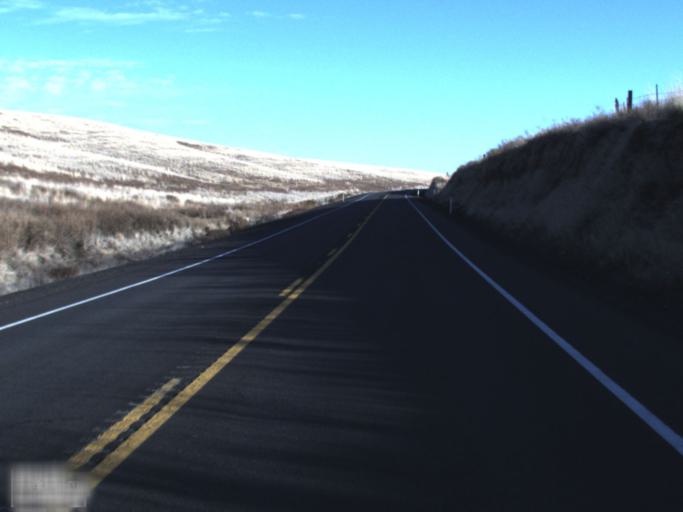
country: US
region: Washington
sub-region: Garfield County
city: Pomeroy
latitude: 46.6953
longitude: -117.7911
